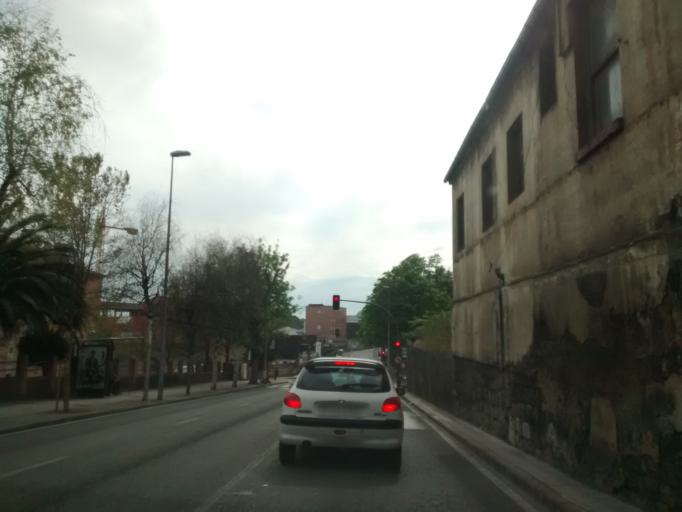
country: ES
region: Cantabria
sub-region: Provincia de Cantabria
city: Santander
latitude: 43.4551
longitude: -3.8336
